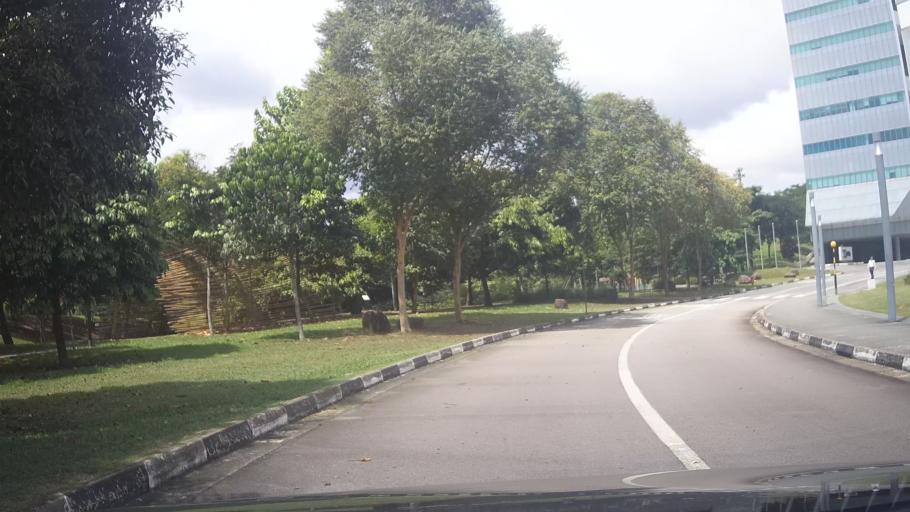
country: MY
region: Johor
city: Johor Bahru
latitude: 1.4433
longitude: 103.7844
